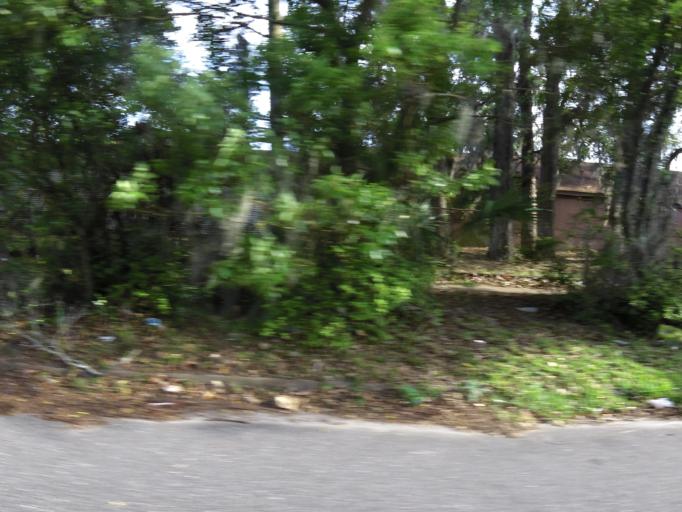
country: US
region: Florida
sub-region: Duval County
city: Jacksonville
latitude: 30.3704
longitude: -81.6525
